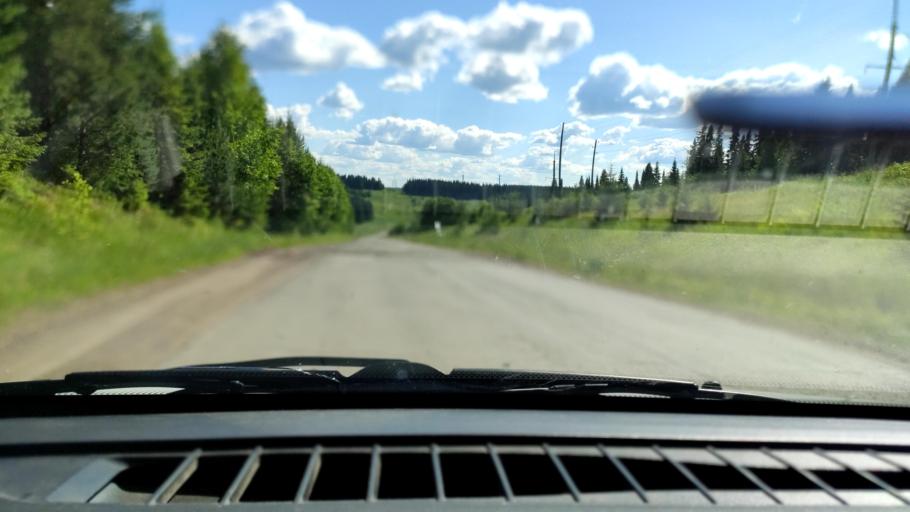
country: RU
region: Perm
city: Uinskoye
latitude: 57.1229
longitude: 56.5539
